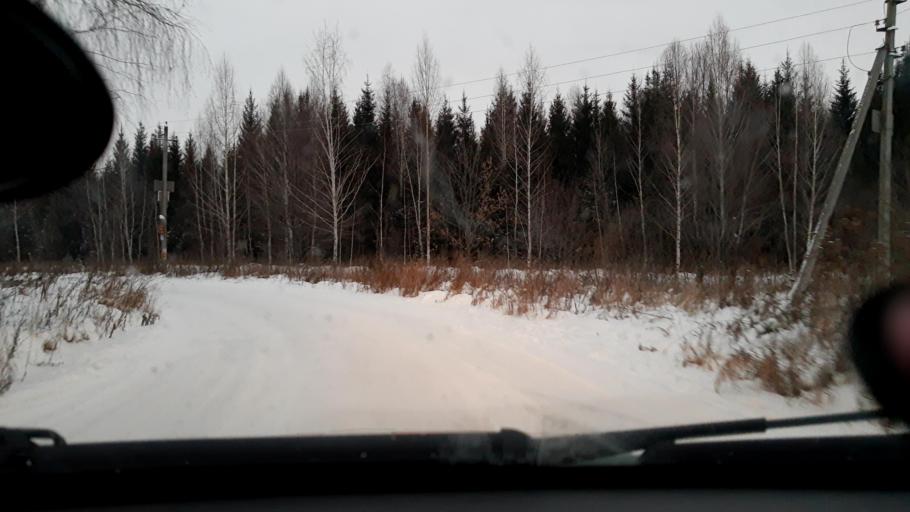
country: RU
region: Bashkortostan
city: Iglino
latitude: 54.8358
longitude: 56.2232
